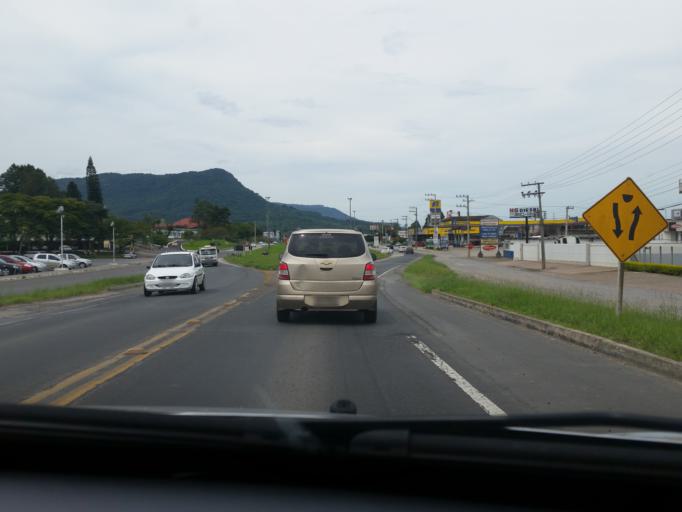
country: BR
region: Santa Catarina
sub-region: Rio Do Sul
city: Rio do Sul
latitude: -27.2031
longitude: -49.6349
